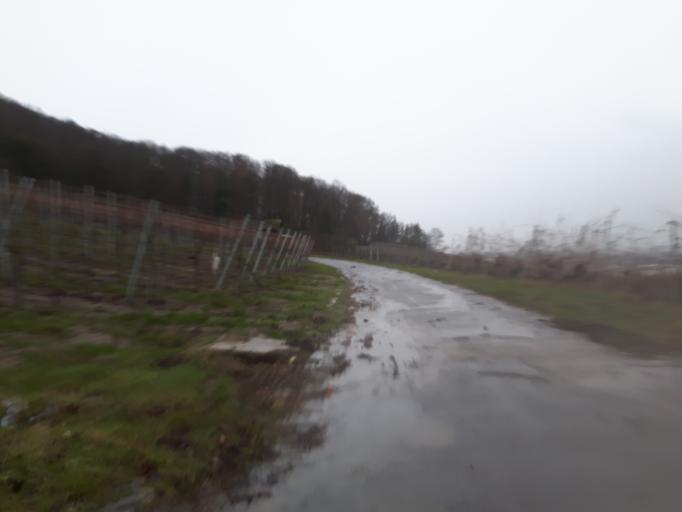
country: DE
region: Baden-Wuerttemberg
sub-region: Regierungsbezirk Stuttgart
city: Heilbronn
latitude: 49.1621
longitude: 9.2401
